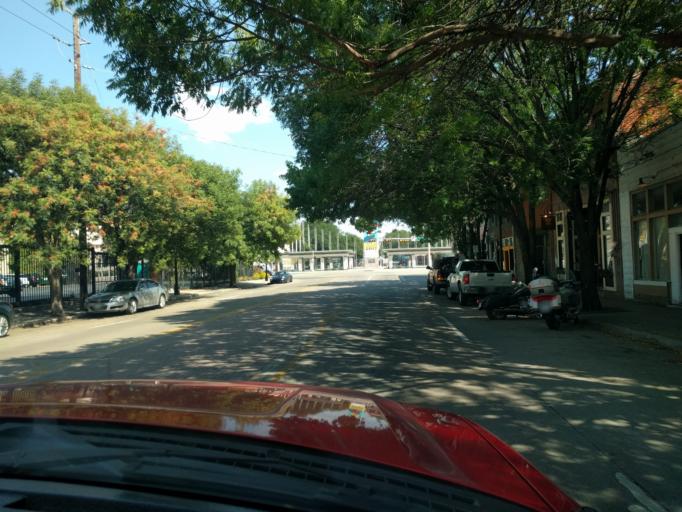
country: US
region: Texas
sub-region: Dallas County
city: Dallas
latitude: 32.7823
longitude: -96.7671
